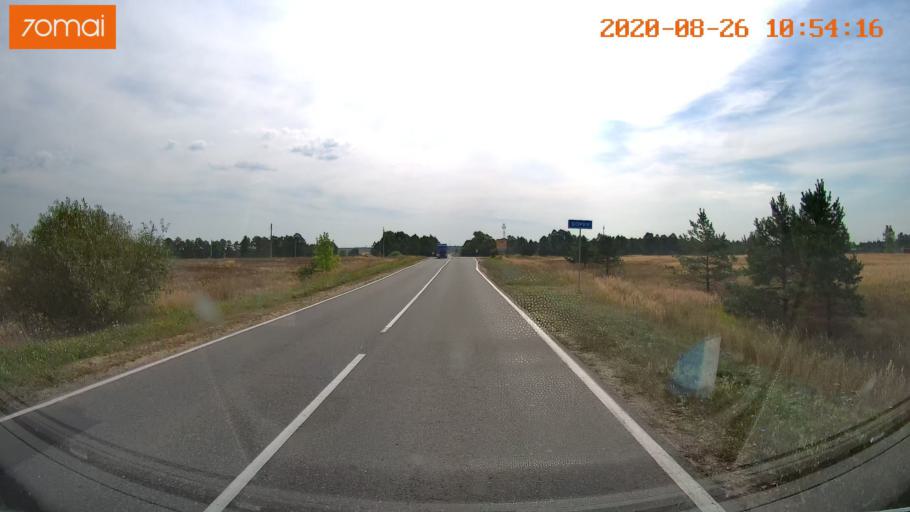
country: RU
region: Rjazan
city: Izhevskoye
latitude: 54.6303
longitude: 41.1591
